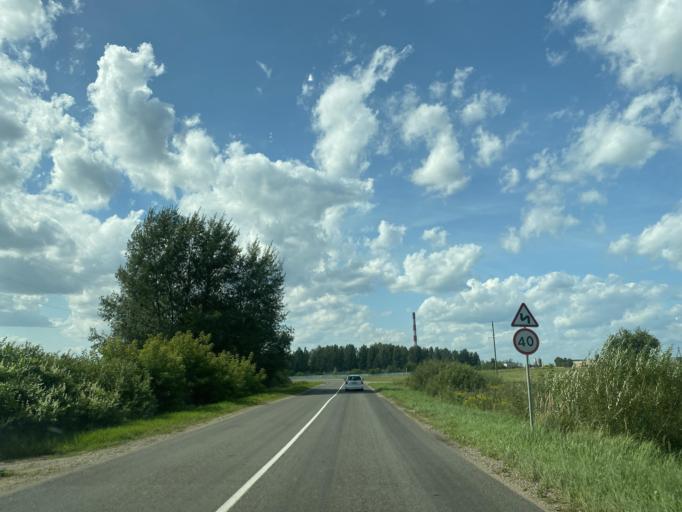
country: BY
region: Minsk
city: Horad Zhodzina
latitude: 54.0859
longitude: 28.3696
